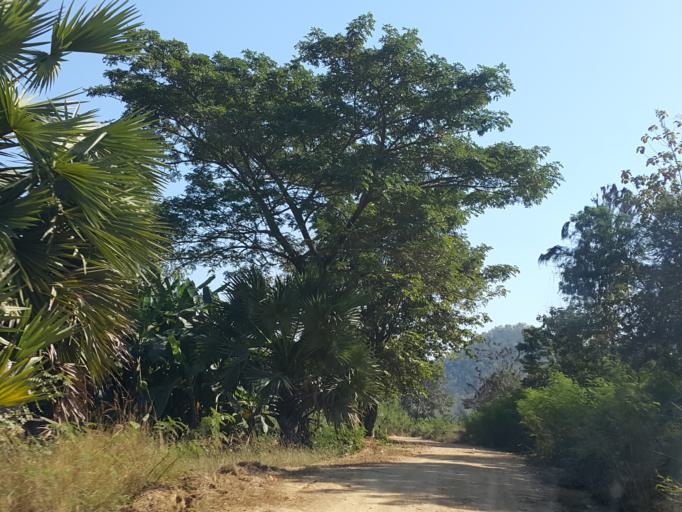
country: TH
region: Sukhothai
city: Thung Saliam
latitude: 17.3151
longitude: 99.4421
